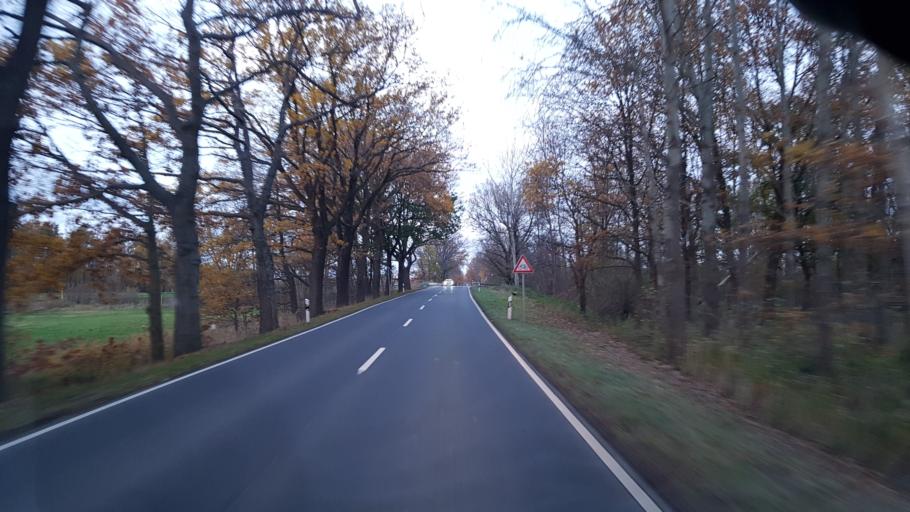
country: DE
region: Brandenburg
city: Schraden
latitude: 51.4579
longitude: 13.7116
